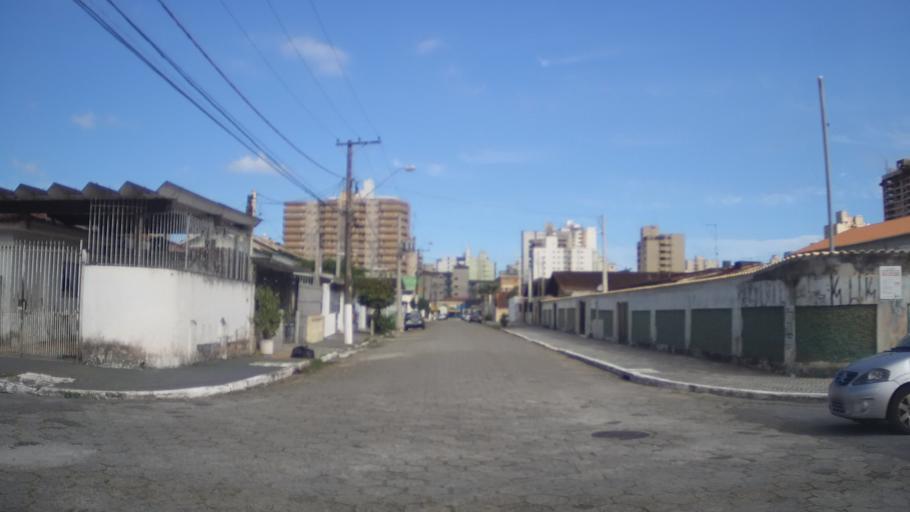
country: BR
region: Sao Paulo
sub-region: Praia Grande
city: Praia Grande
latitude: -24.0157
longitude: -46.4582
